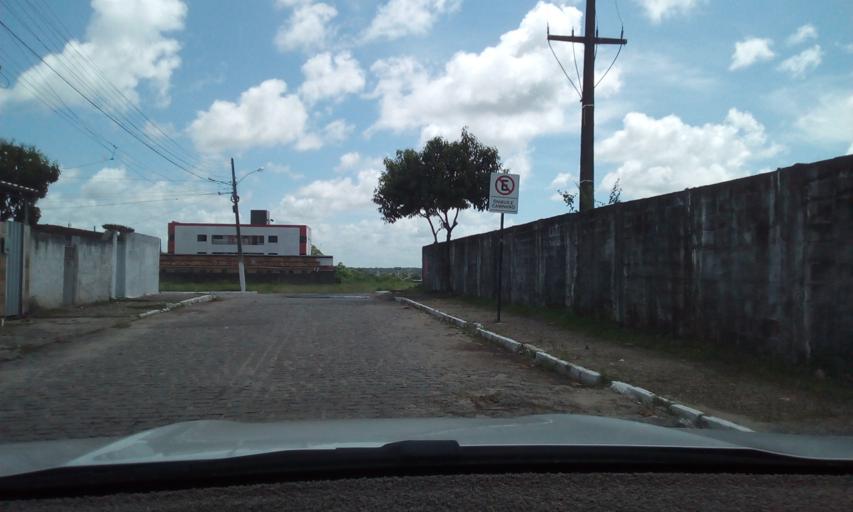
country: BR
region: Paraiba
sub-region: Joao Pessoa
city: Joao Pessoa
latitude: -7.1683
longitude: -34.8895
